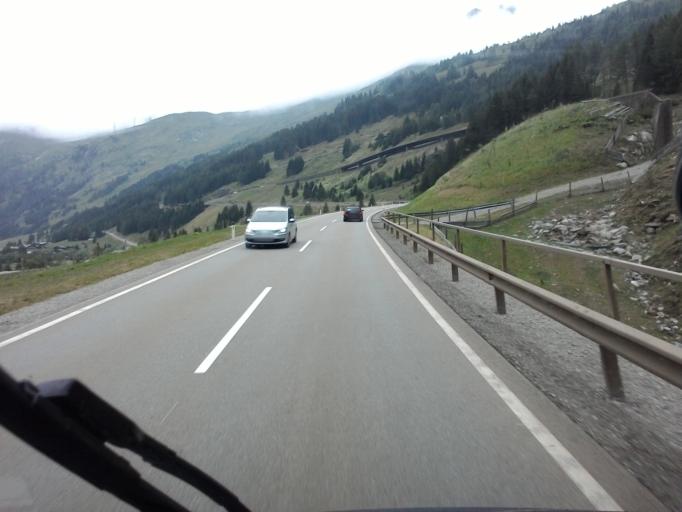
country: AT
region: Tyrol
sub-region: Politischer Bezirk Lienz
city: Matrei in Osttirol
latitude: 47.1123
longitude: 12.5040
